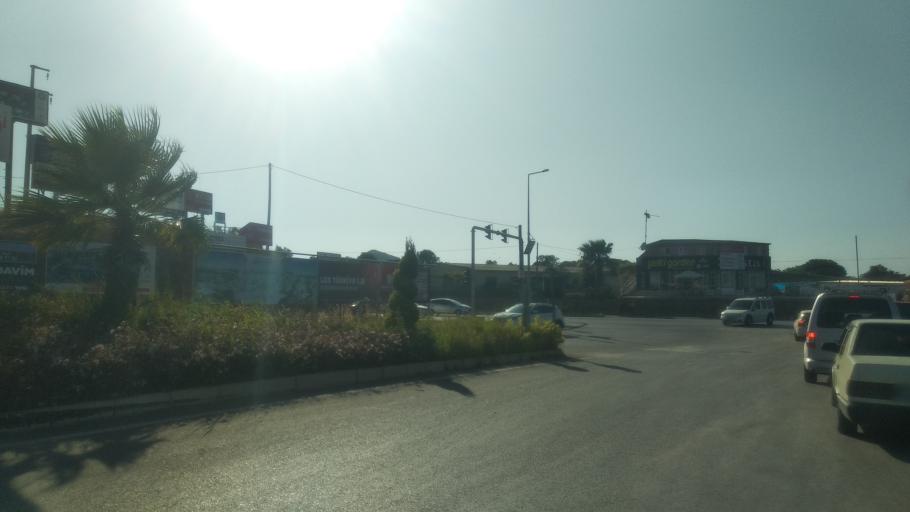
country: TR
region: Izmir
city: Urla
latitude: 38.3553
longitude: 26.8702
